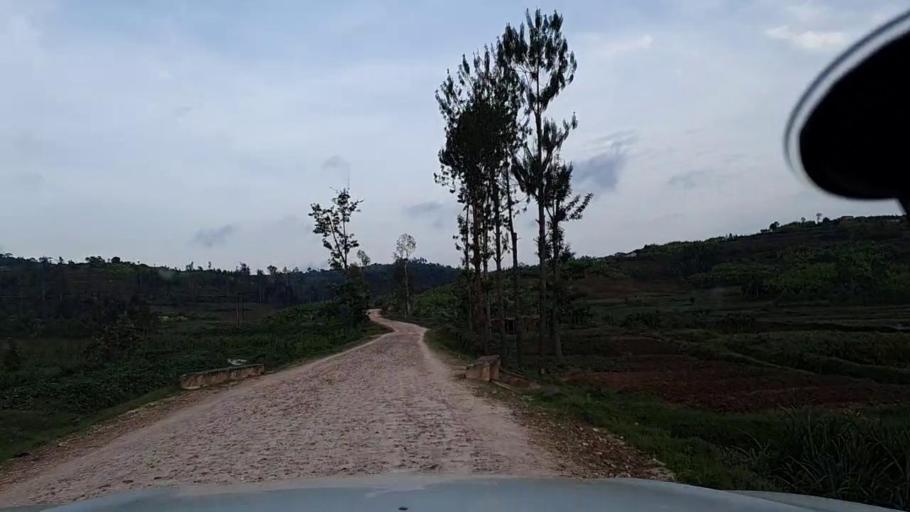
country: RW
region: Southern Province
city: Nyanza
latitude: -2.2138
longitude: 29.6202
